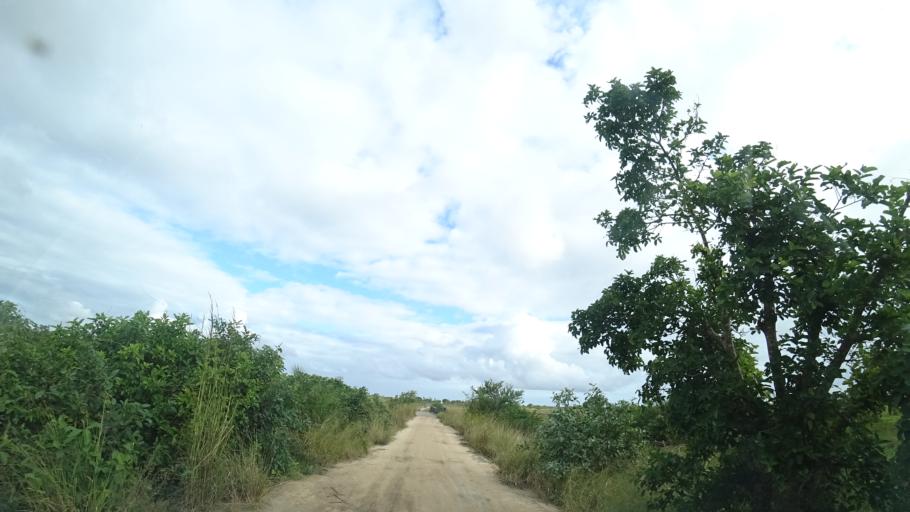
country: MZ
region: Sofala
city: Beira
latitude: -19.6294
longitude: 35.0601
